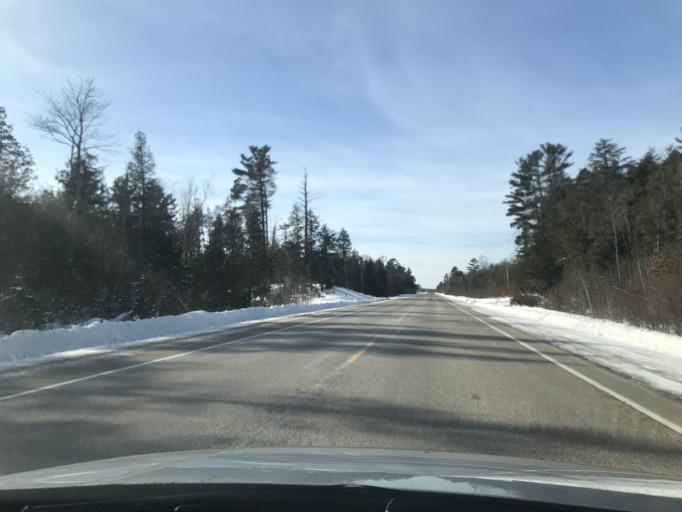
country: US
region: Wisconsin
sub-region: Oconto County
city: Gillett
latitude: 45.1144
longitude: -88.3446
